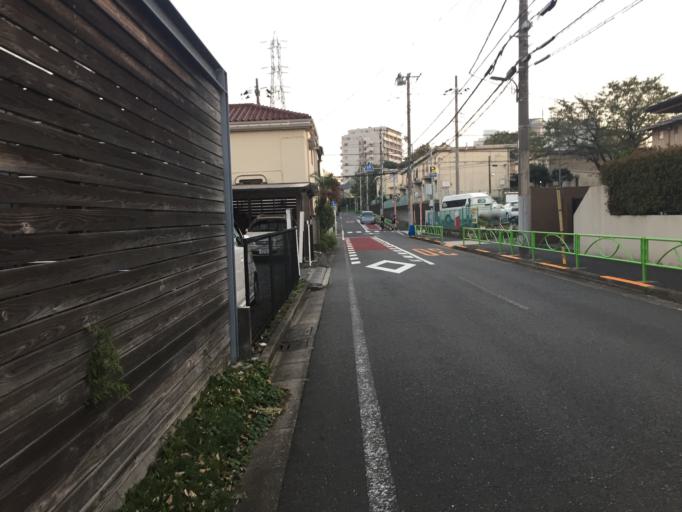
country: JP
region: Tokyo
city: Tokyo
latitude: 35.6302
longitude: 139.6653
